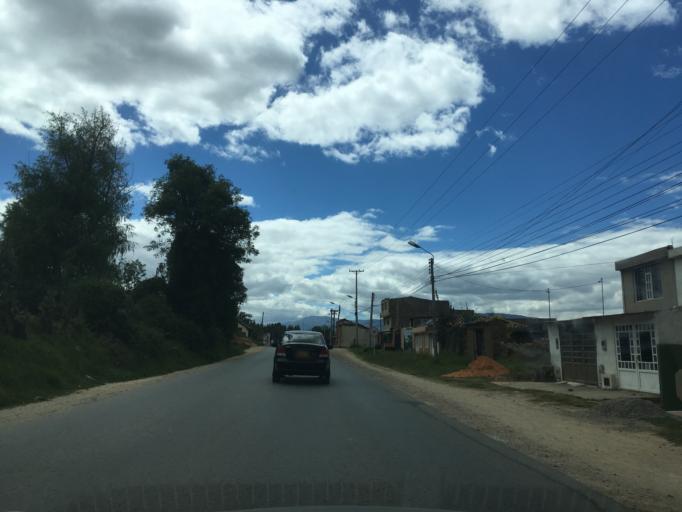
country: CO
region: Boyaca
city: Sogamoso
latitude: 5.6851
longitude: -72.9509
